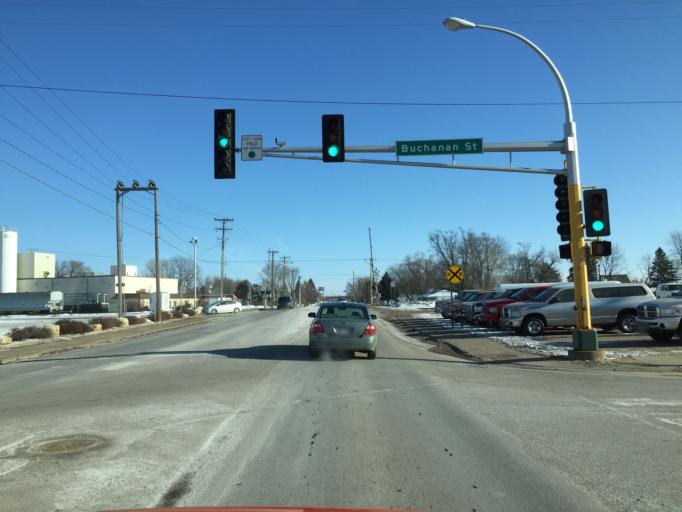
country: US
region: Minnesota
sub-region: Isanti County
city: Cambridge
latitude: 45.5727
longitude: -93.2217
